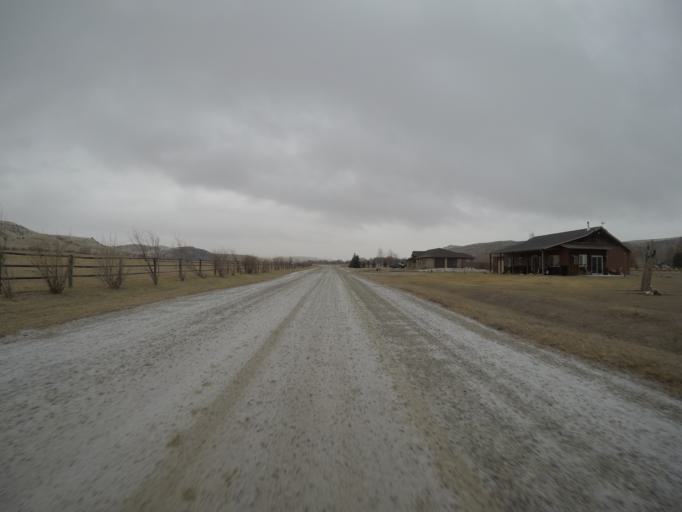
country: US
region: Montana
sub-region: Stillwater County
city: Absarokee
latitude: 45.5272
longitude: -109.4677
